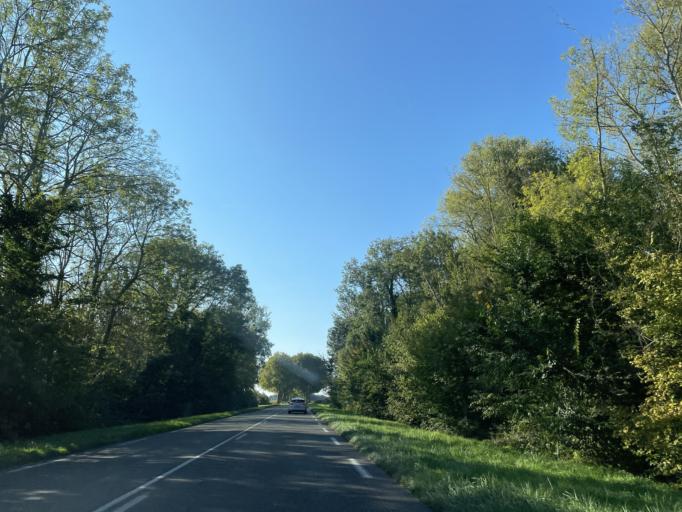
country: FR
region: Ile-de-France
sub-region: Departement de Seine-et-Marne
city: Guerard
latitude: 48.8379
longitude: 2.9766
